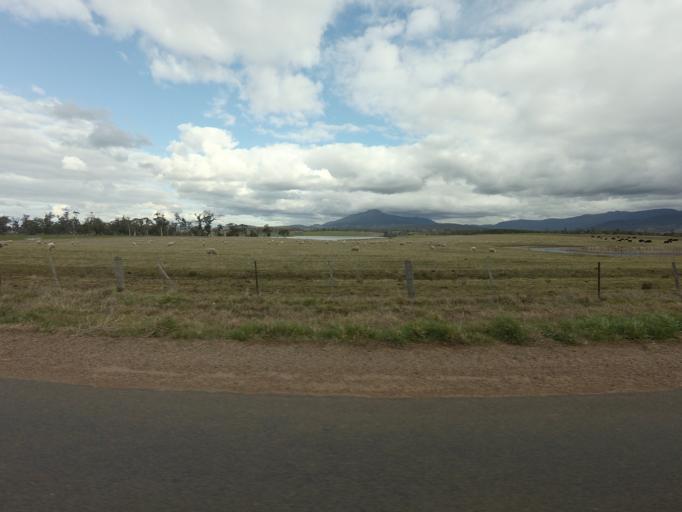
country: AU
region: Tasmania
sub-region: Northern Midlands
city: Longford
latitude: -41.8059
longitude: 147.1575
